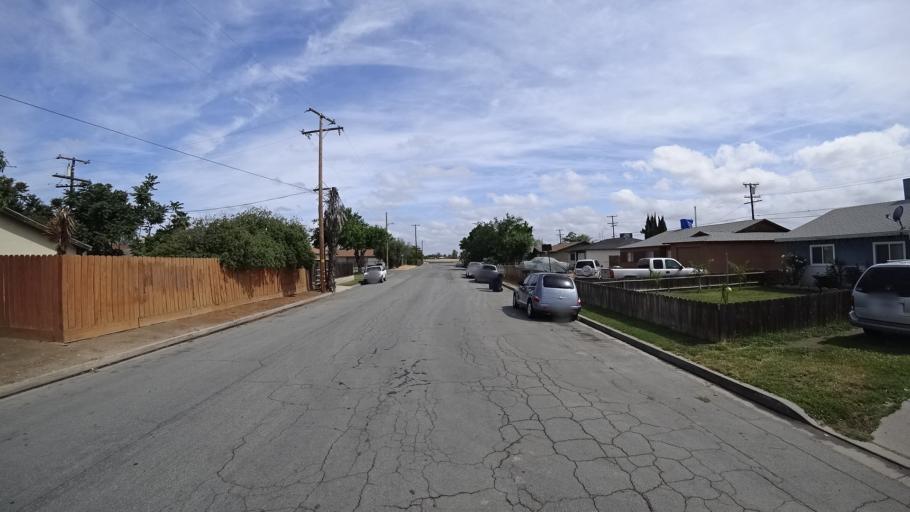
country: US
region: California
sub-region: Kings County
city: Home Garden
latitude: 36.3044
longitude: -119.6509
